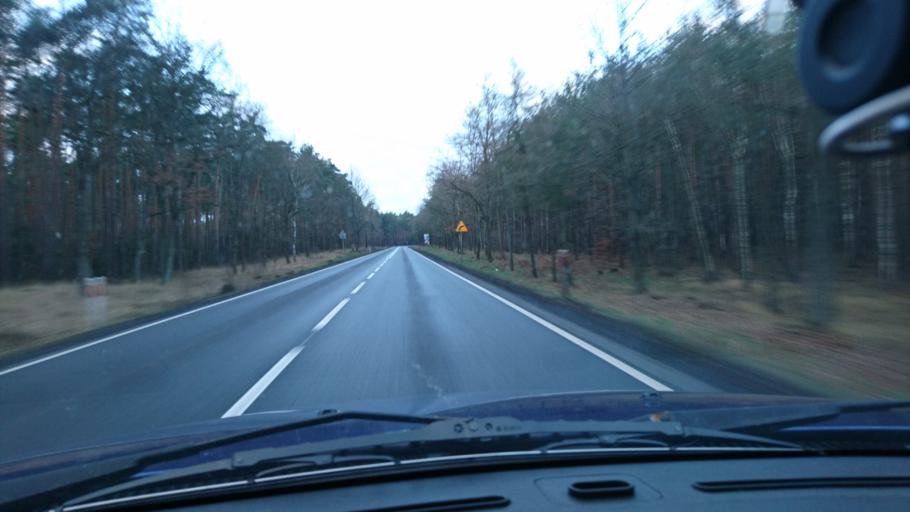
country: PL
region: Greater Poland Voivodeship
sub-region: Powiat kepinski
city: Kepno
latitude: 51.3350
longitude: 17.9556
